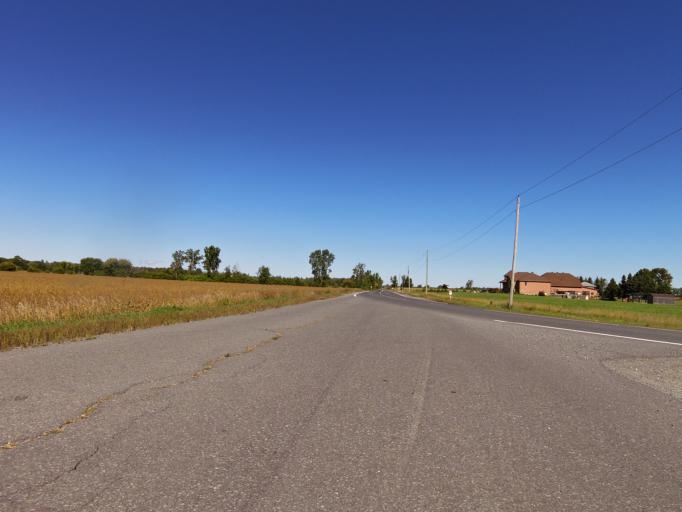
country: CA
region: Ontario
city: Clarence-Rockland
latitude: 45.3187
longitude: -75.4105
